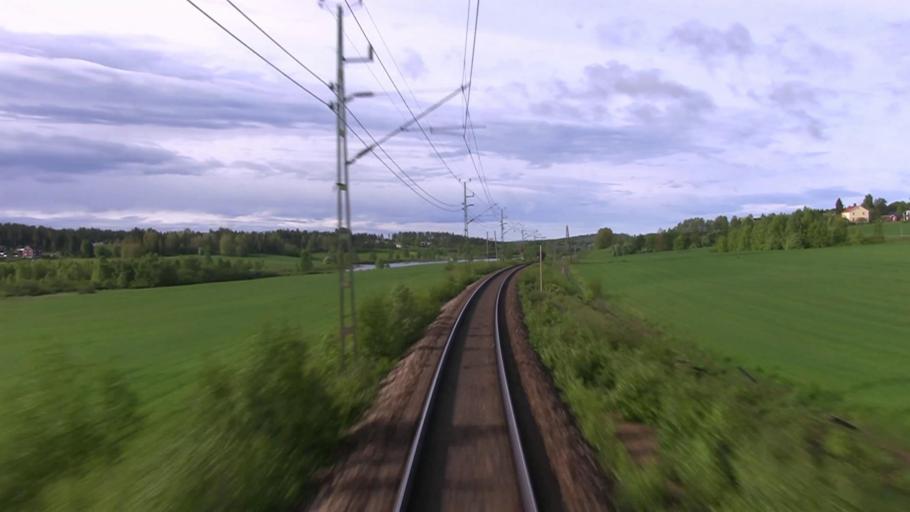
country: SE
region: Vaesterbotten
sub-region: Vindelns Kommun
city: Vindeln
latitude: 64.1054
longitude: 19.6838
